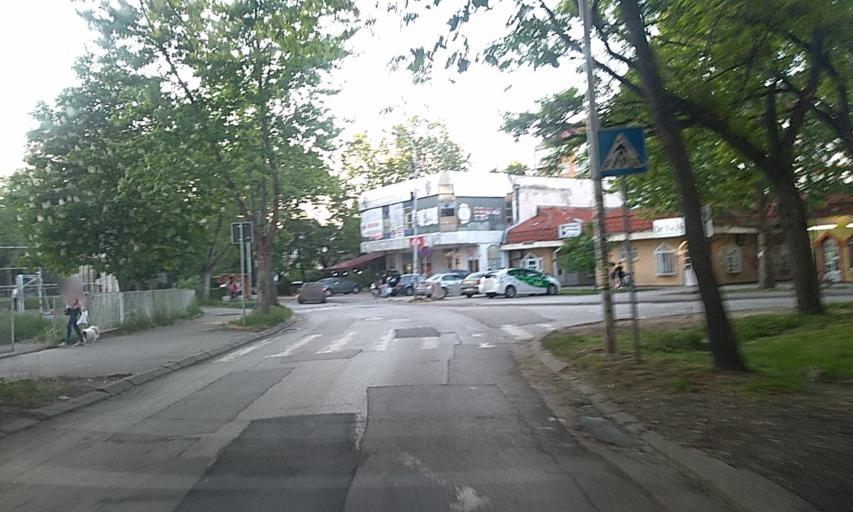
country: RS
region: Central Serbia
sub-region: Nisavski Okrug
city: Nis
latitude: 43.3224
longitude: 21.9209
